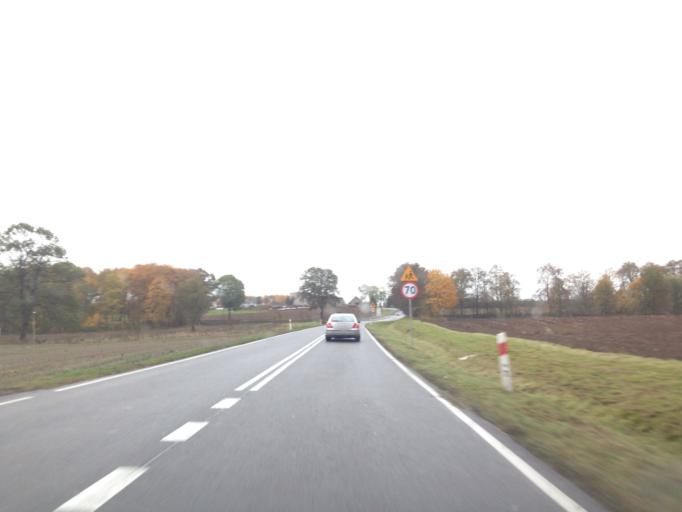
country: PL
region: Warmian-Masurian Voivodeship
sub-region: Powiat nowomiejski
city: Biskupiec
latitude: 53.5961
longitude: 19.4302
